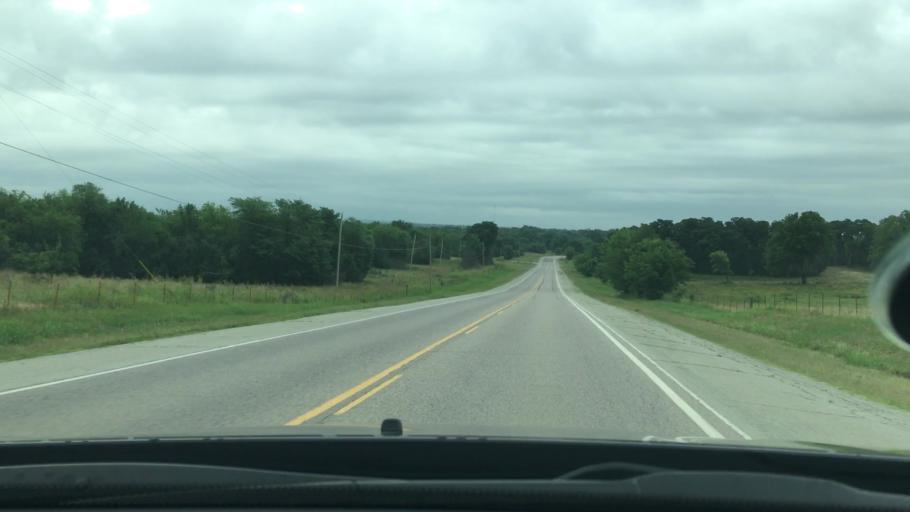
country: US
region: Oklahoma
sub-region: Coal County
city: Coalgate
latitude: 34.5526
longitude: -96.2368
